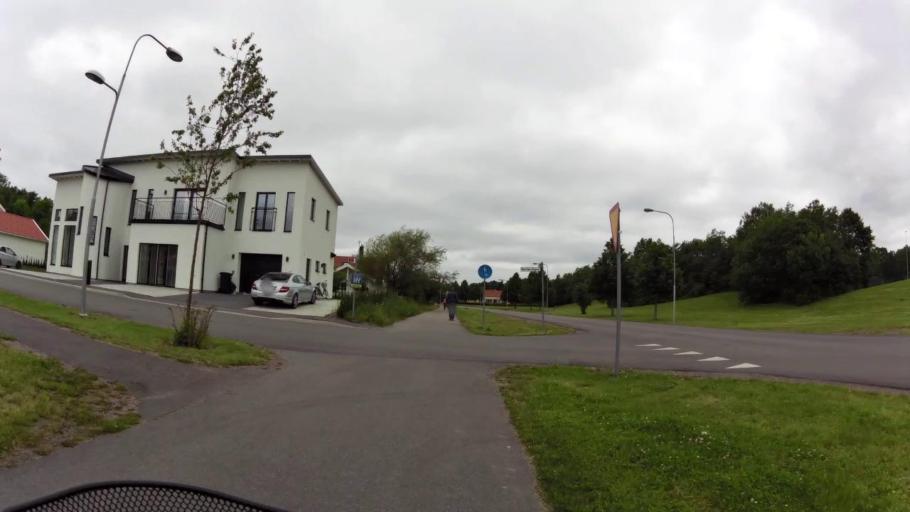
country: SE
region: OEstergoetland
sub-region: Linkopings Kommun
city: Sturefors
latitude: 58.3674
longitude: 15.6898
